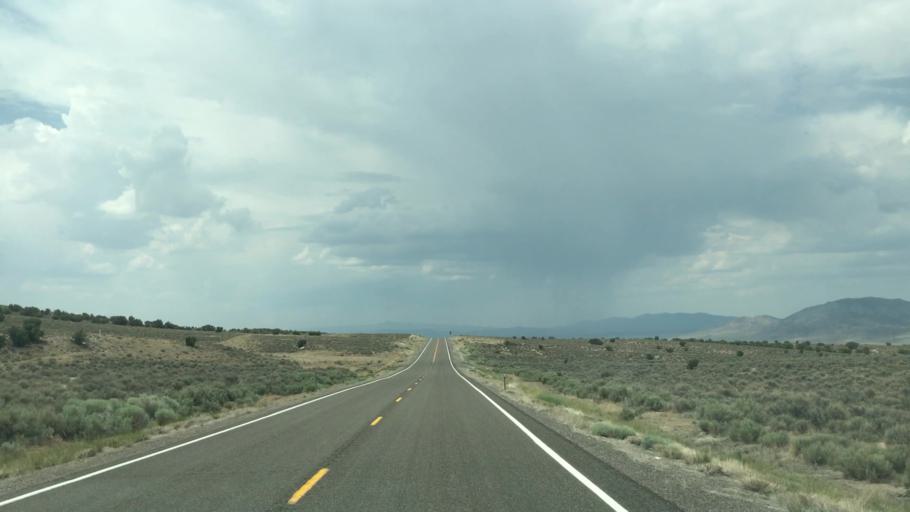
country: US
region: Nevada
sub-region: Eureka County
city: Eureka
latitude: 39.3970
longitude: -115.7154
